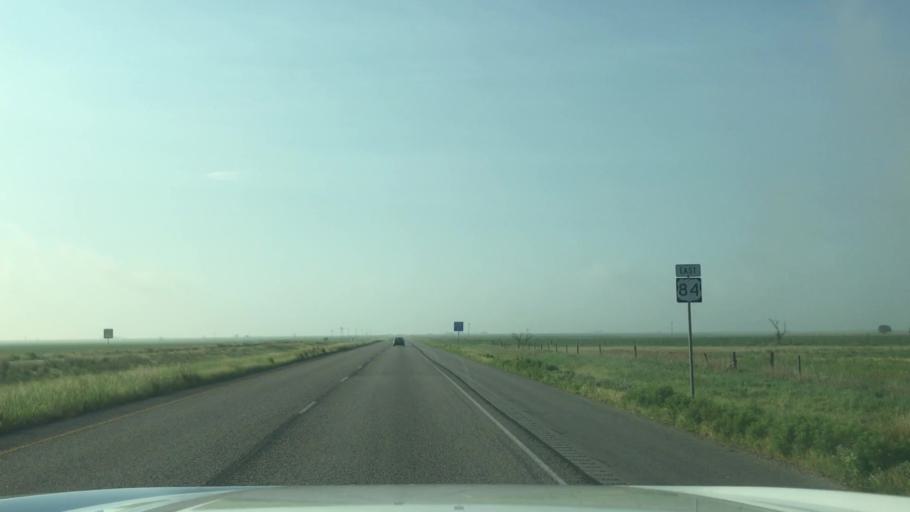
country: US
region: Texas
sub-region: Lubbock County
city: Slaton
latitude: 33.3358
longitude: -101.5379
